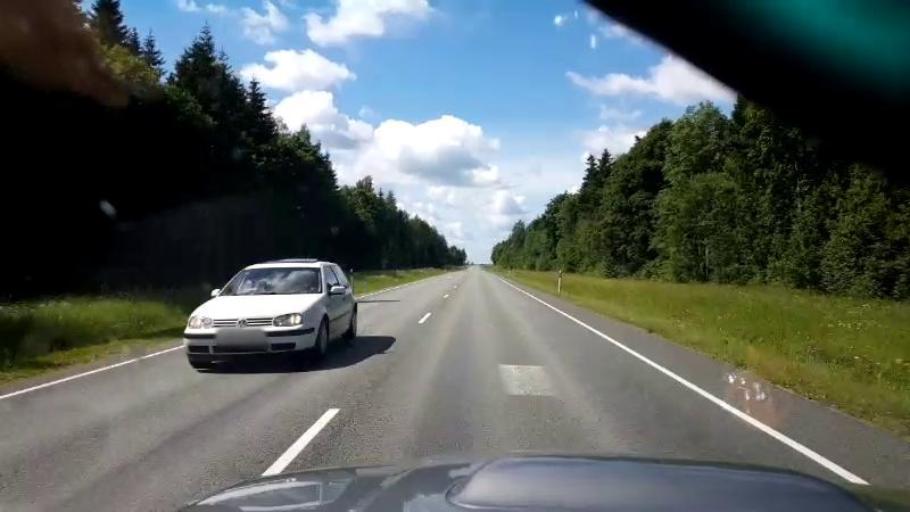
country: EE
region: Jaervamaa
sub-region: Jaerva-Jaani vald
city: Jarva-Jaani
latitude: 59.1843
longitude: 25.7959
